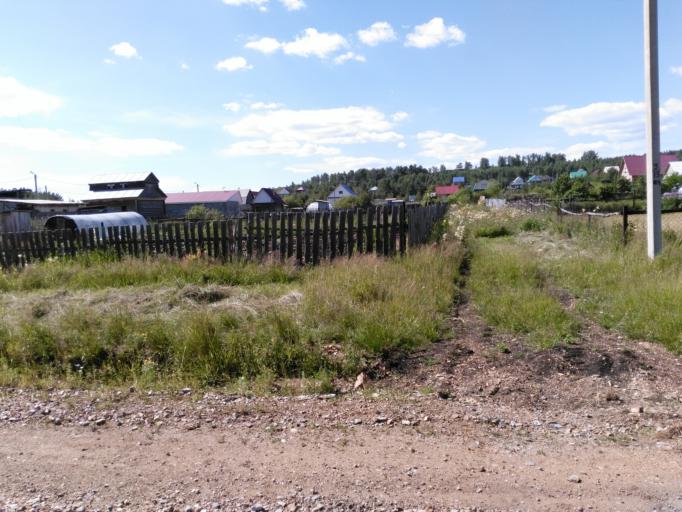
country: RU
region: Bashkortostan
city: Uchaly
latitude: 54.2879
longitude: 59.3597
